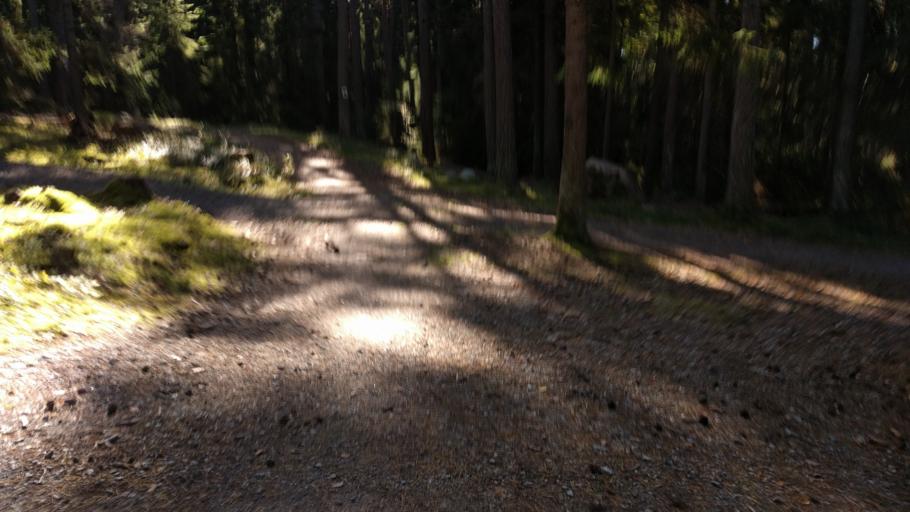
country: SE
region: Stockholm
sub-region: Vallentuna Kommun
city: Vallentuna
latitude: 59.4954
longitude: 18.1066
